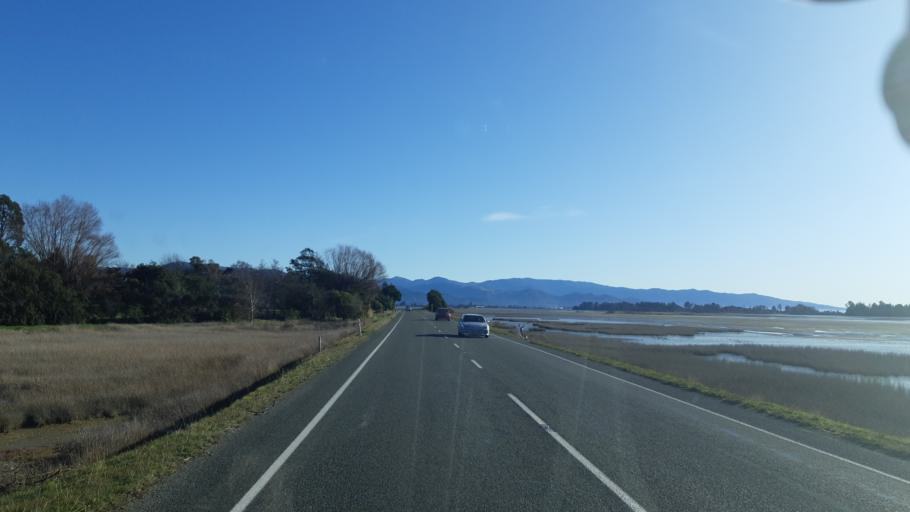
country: NZ
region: Tasman
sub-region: Tasman District
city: Motueka
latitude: -41.1711
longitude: 173.0338
